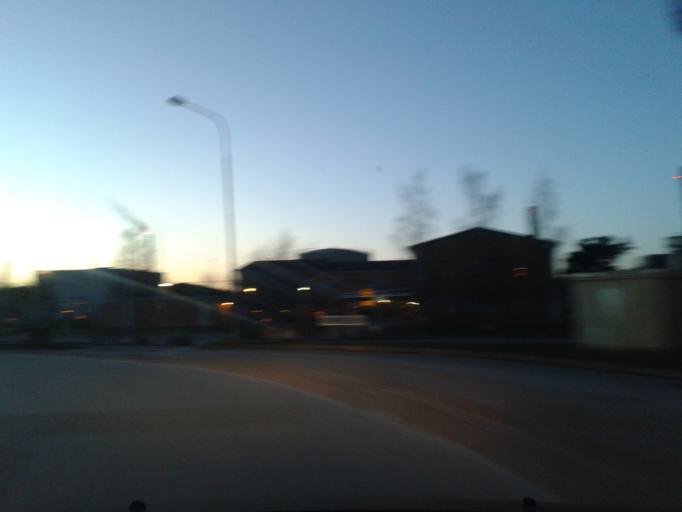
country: SE
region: Gotland
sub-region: Gotland
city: Visby
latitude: 57.6231
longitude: 18.3224
